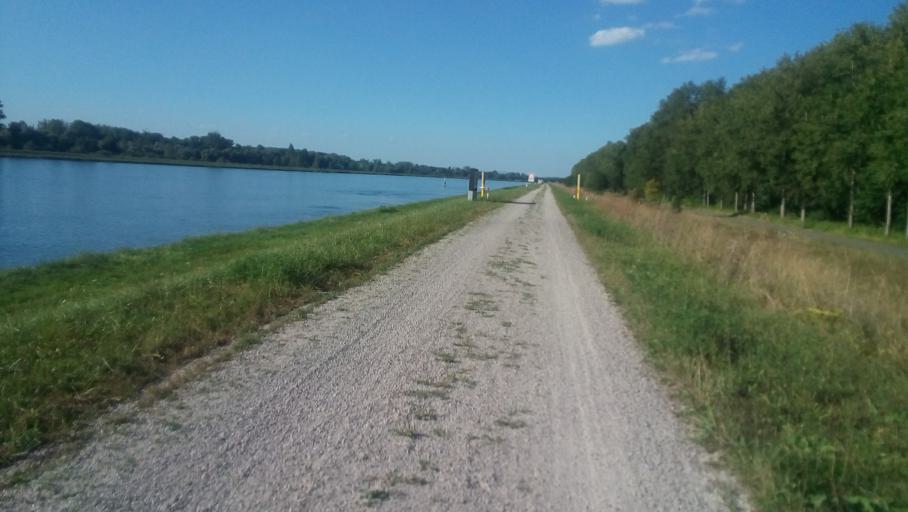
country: DE
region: Baden-Wuerttemberg
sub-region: Karlsruhe Region
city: Lichtenau
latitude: 48.7330
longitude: 7.9696
